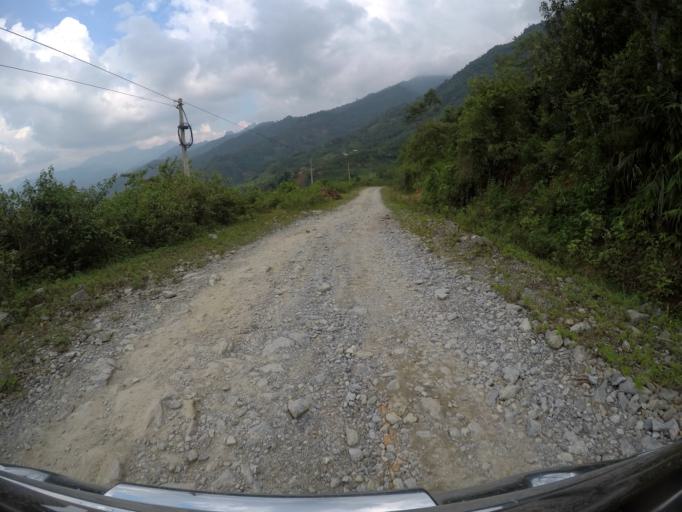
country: VN
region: Yen Bai
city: Son Thinh
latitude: 21.6846
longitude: 104.5749
